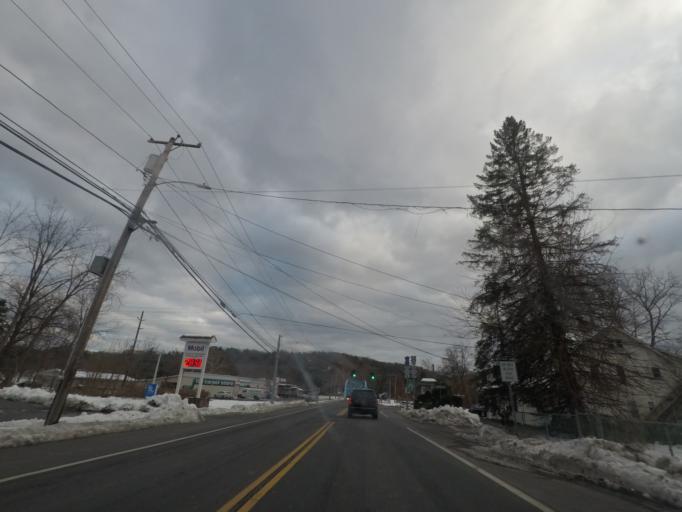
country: US
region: New York
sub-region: Ulster County
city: Rosendale Village
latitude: 41.8481
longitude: -74.0751
